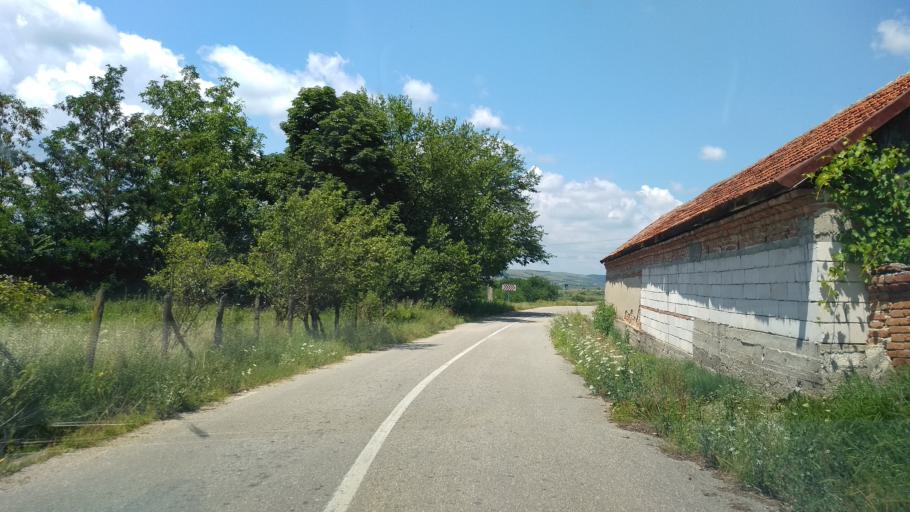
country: RO
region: Hunedoara
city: Berca
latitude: 45.6246
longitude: 23.0222
